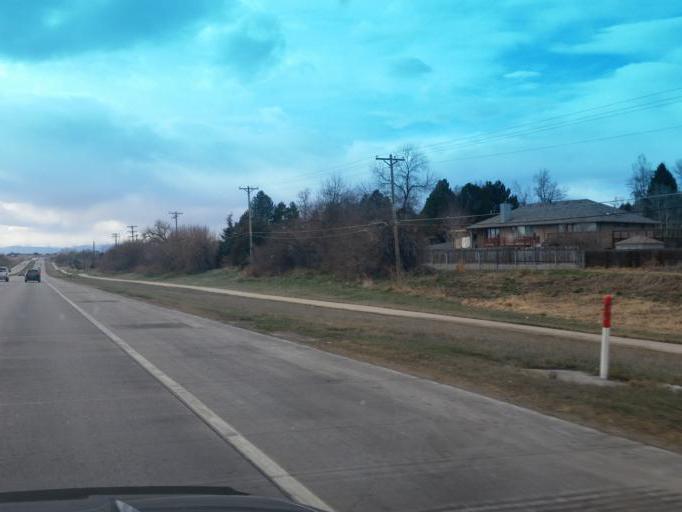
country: US
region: Colorado
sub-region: Weld County
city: Greeley
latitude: 40.3922
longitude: -104.7627
